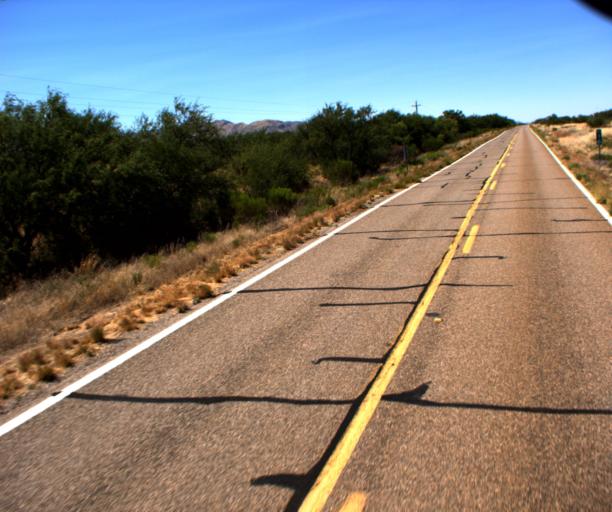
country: US
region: Arizona
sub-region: Pima County
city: Three Points
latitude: 31.6998
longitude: -111.4873
